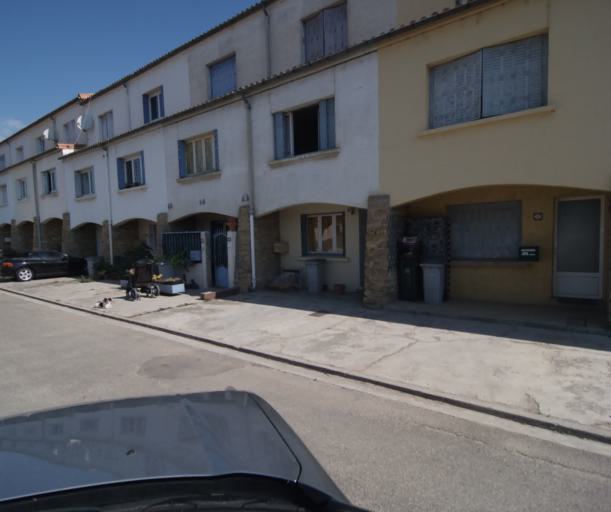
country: FR
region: Languedoc-Roussillon
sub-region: Departement de l'Aude
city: Limoux
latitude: 43.0668
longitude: 2.2199
